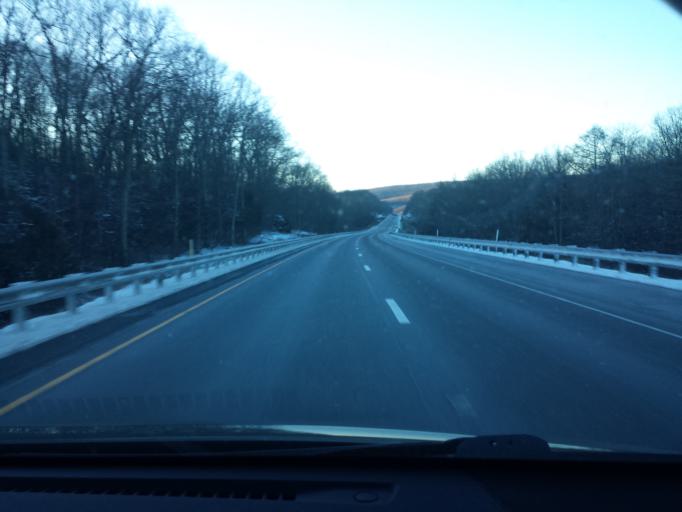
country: US
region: Pennsylvania
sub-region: Clinton County
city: Castanea
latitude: 41.0521
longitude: -77.3479
